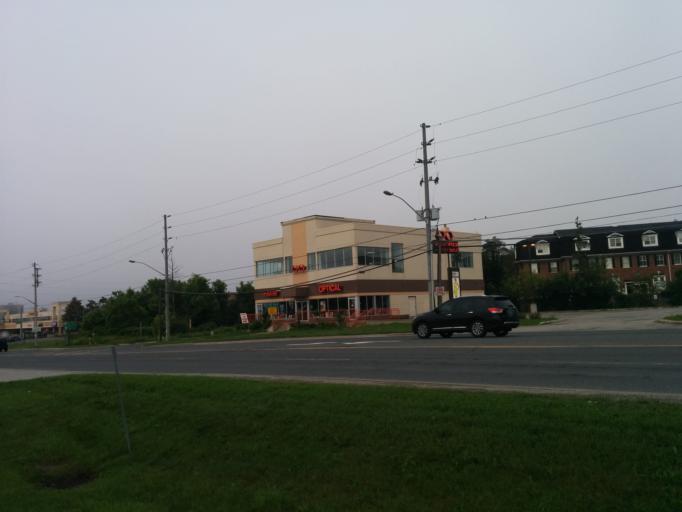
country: CA
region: Ontario
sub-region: York
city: Richmond Hill
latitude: 43.8911
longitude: -79.4417
